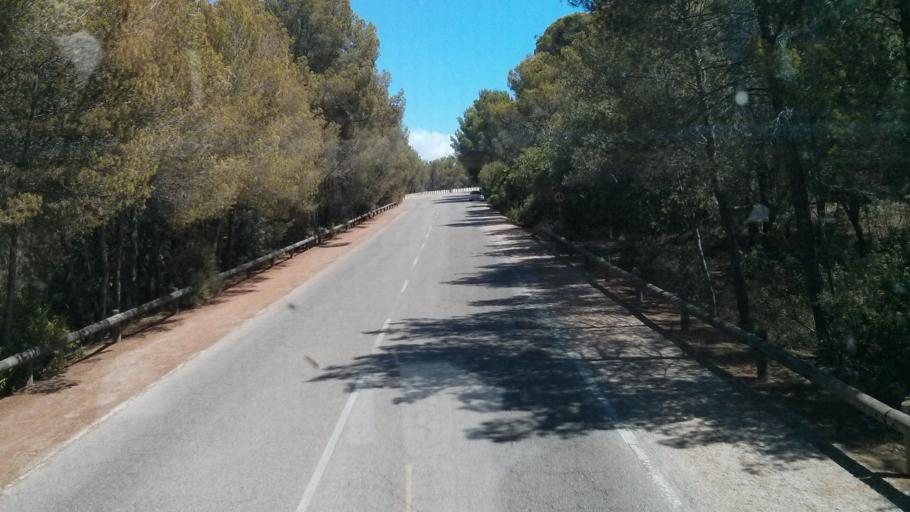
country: ES
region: Balearic Islands
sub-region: Illes Balears
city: Palma
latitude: 39.5652
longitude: 2.6169
